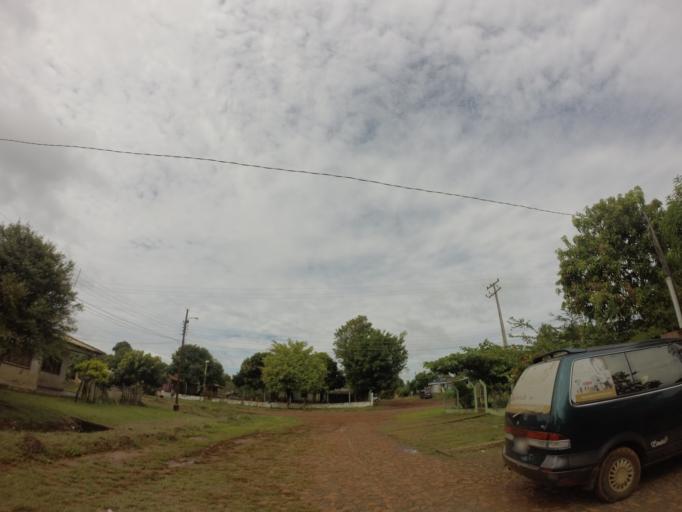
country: PY
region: Alto Parana
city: Ciudad del Este
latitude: -25.4024
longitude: -54.6530
